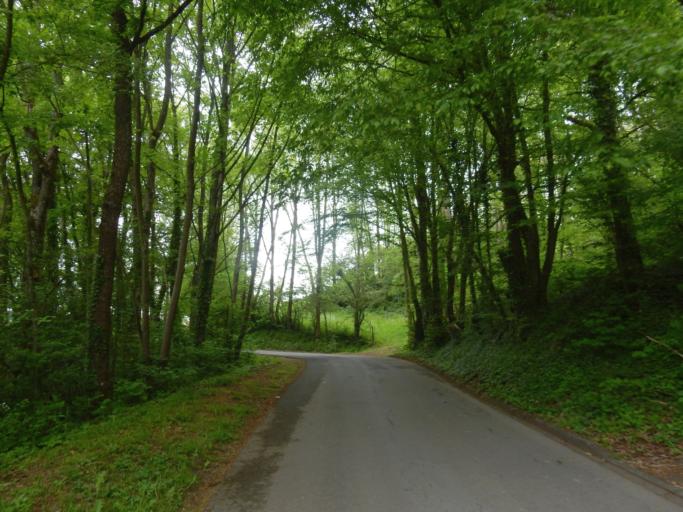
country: LU
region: Diekirch
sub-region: Canton de Diekirch
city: Diekirch
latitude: 49.8761
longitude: 6.1565
